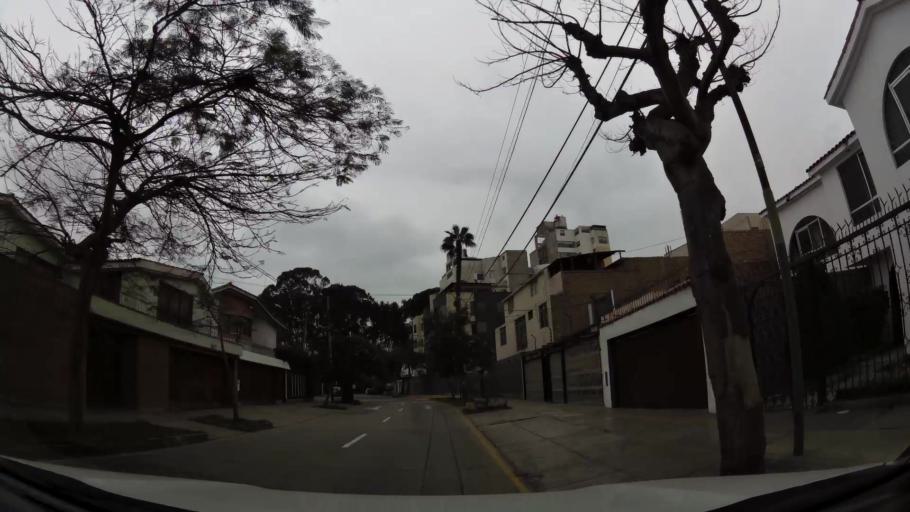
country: PE
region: Lima
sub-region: Lima
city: San Luis
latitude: -12.0952
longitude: -77.0000
